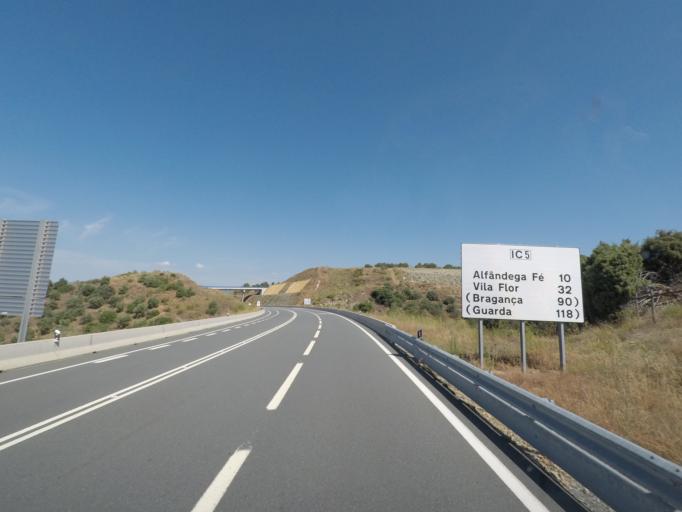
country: PT
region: Braganca
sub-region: Alfandega da Fe
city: Alfandega da Fe
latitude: 41.2852
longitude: -6.8936
